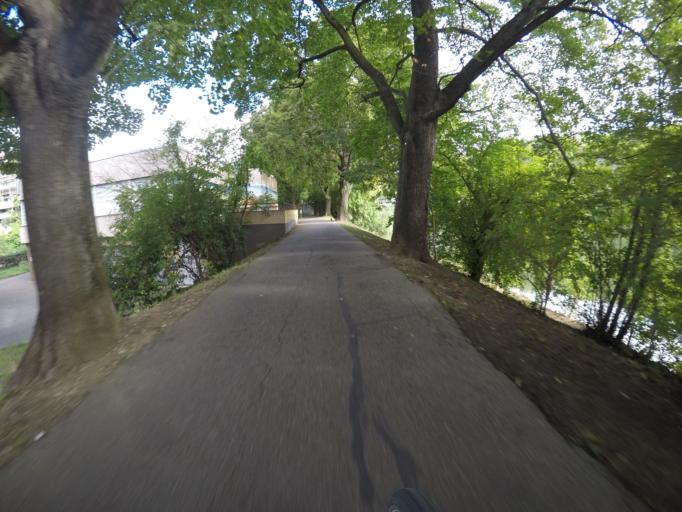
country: DE
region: Baden-Wuerttemberg
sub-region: Regierungsbezirk Stuttgart
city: Stuttgart Muehlhausen
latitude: 48.8192
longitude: 9.2273
